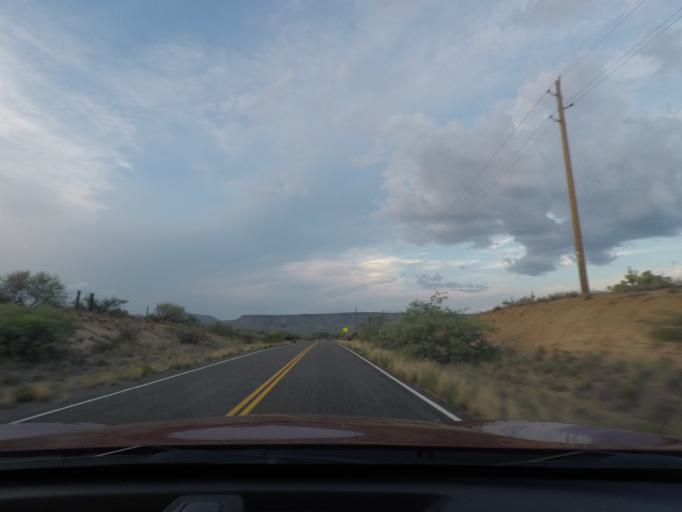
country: US
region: Arizona
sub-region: Yavapai County
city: Bagdad
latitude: 34.4678
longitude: -112.8932
